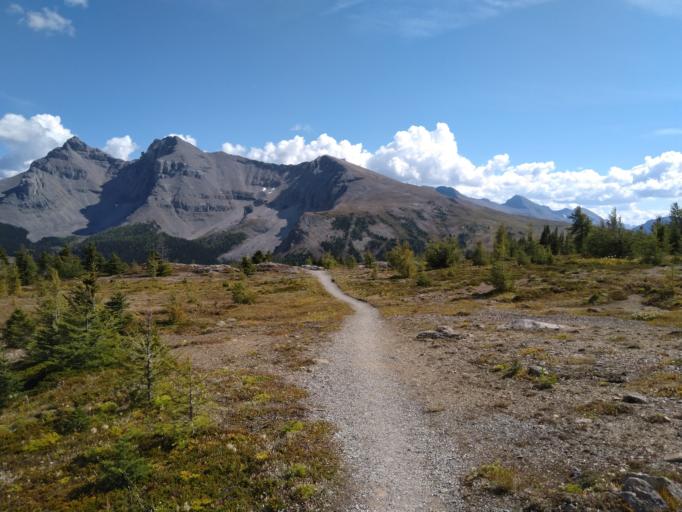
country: CA
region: Alberta
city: Banff
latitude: 51.0845
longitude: -115.7915
